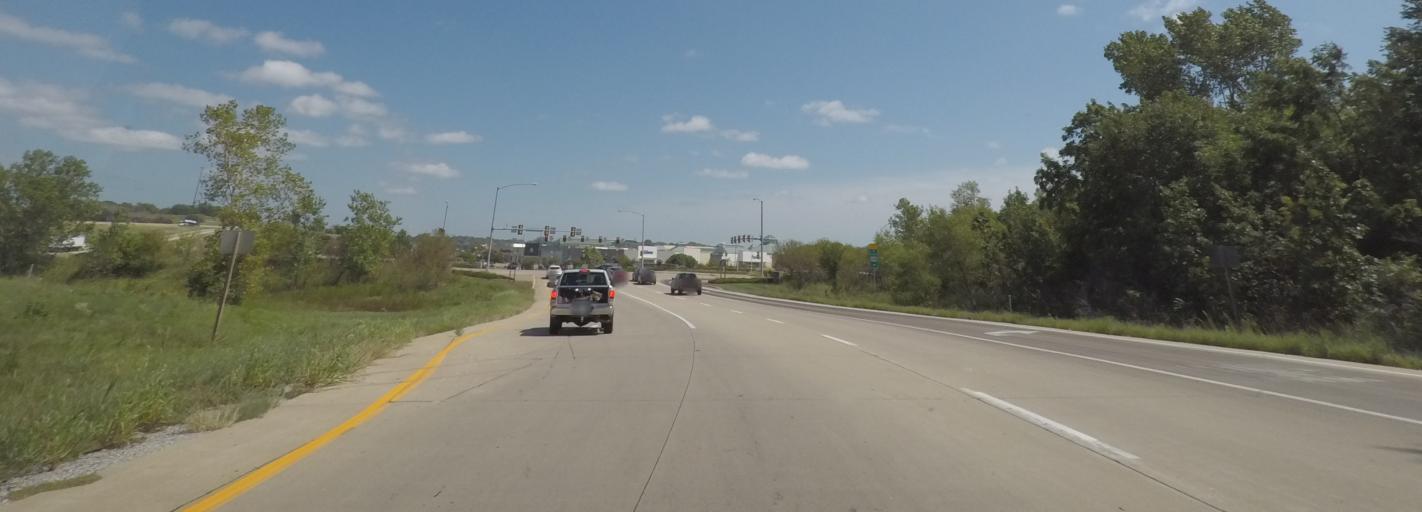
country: US
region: Iowa
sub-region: Johnson County
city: Coralville
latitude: 41.6922
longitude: -91.6101
